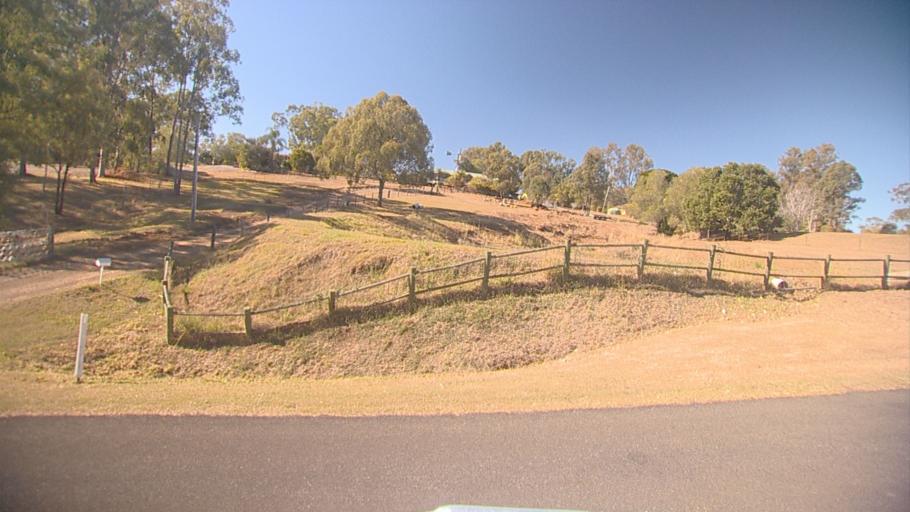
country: AU
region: Queensland
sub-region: Logan
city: Cedar Vale
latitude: -27.8907
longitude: 152.9773
